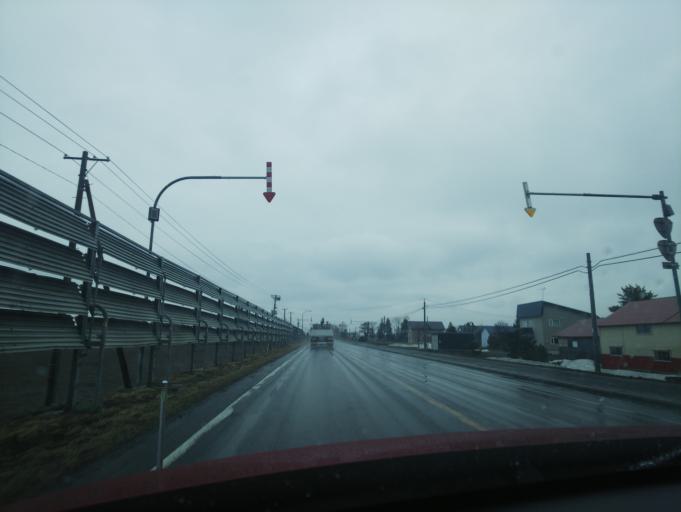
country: JP
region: Hokkaido
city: Nayoro
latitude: 44.1994
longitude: 142.3949
